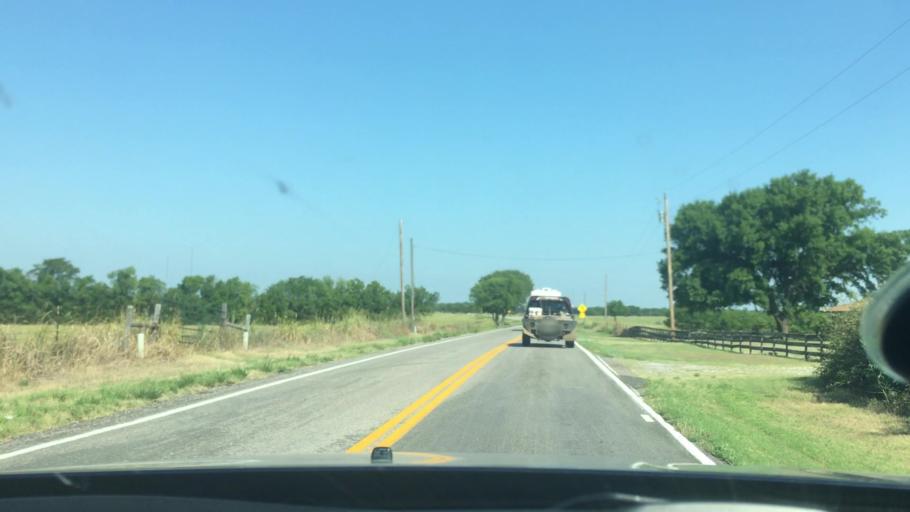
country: US
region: Oklahoma
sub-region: Johnston County
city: Tishomingo
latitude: 34.1846
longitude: -96.5150
